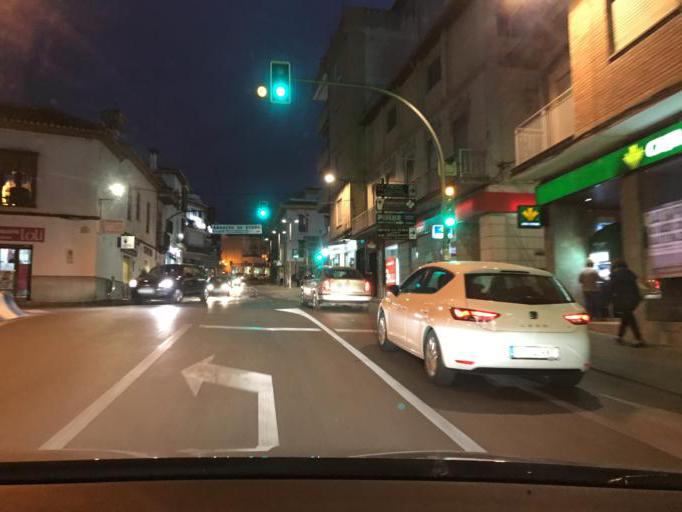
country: ES
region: Andalusia
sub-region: Provincia de Granada
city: Zubia
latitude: 37.1200
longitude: -3.5846
